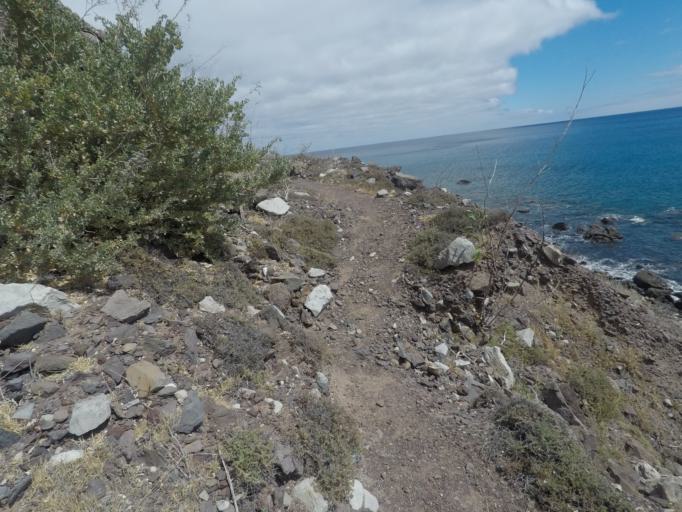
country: PT
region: Madeira
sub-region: Porto Santo
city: Vila de Porto Santo
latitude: 33.0607
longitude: -16.3007
